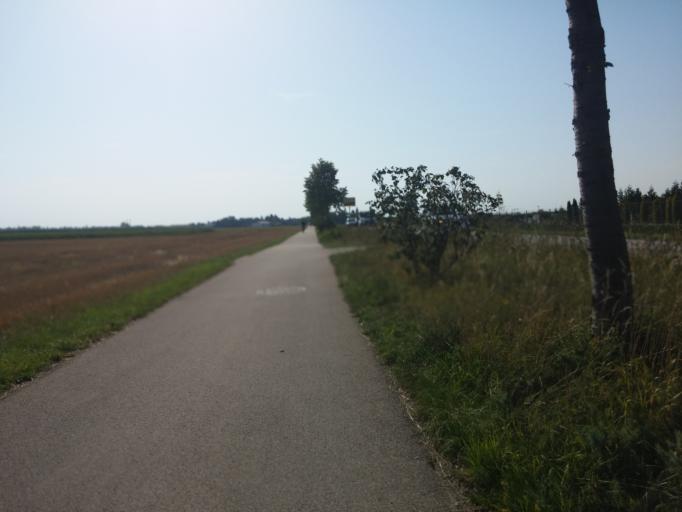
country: DE
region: Bavaria
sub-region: Upper Bavaria
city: Feldkirchen
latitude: 48.1302
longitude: 11.7346
